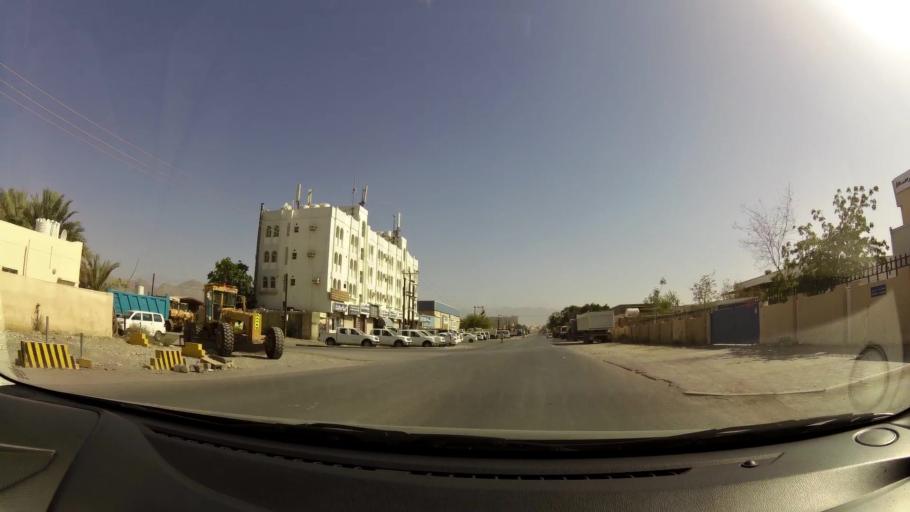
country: OM
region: Muhafazat Masqat
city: Bawshar
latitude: 23.5756
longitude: 58.3603
